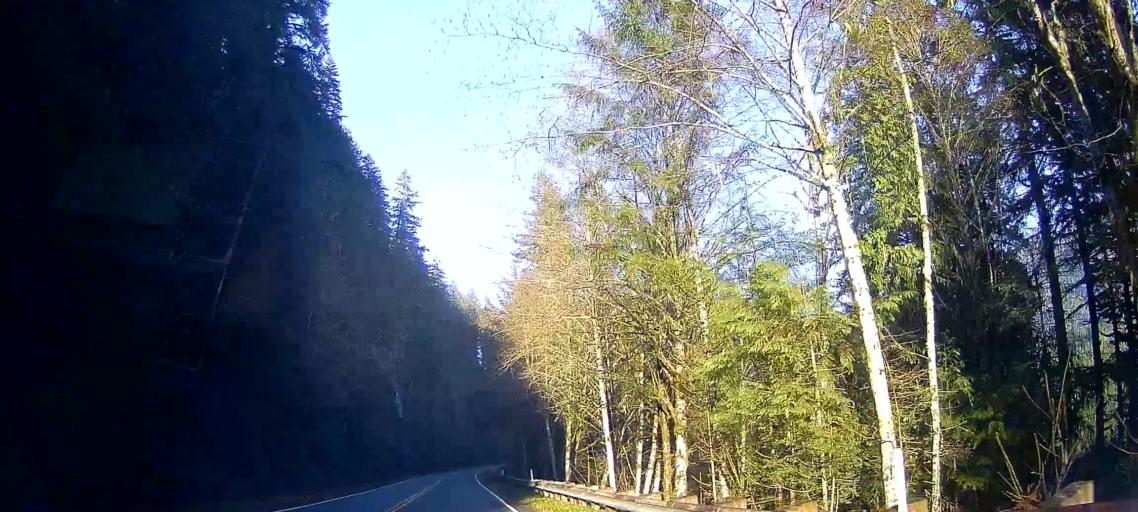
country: US
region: Washington
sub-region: Snohomish County
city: Darrington
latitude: 48.6495
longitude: -121.7121
